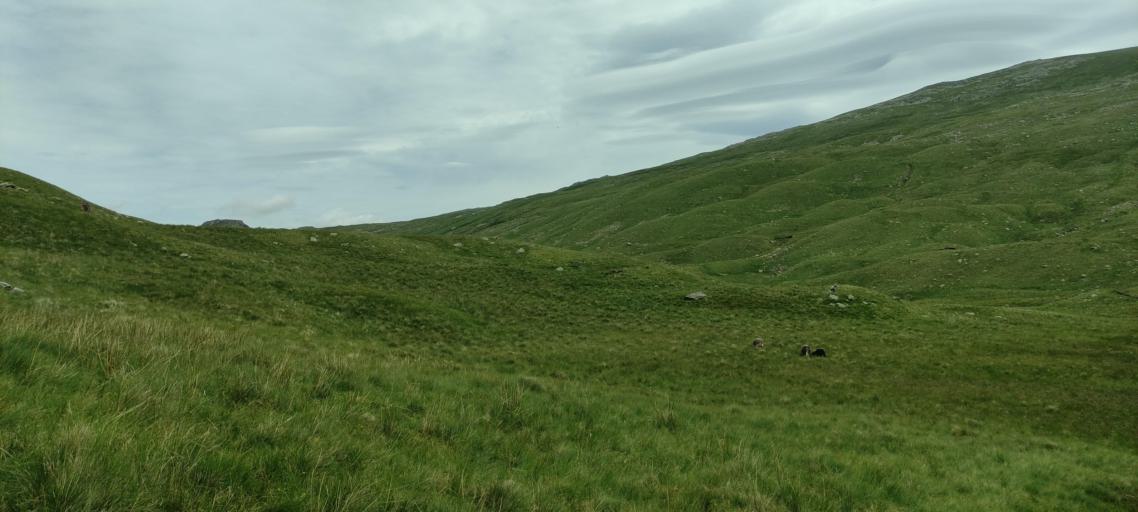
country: GB
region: England
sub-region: Cumbria
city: Keswick
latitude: 54.4709
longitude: -3.1337
